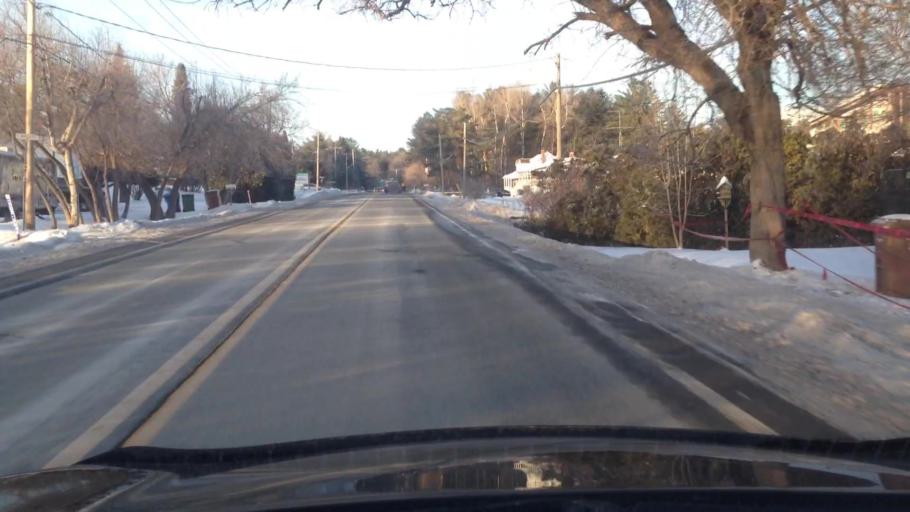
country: CA
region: Quebec
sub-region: Lanaudiere
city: Sainte-Julienne
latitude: 45.9208
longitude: -73.7389
